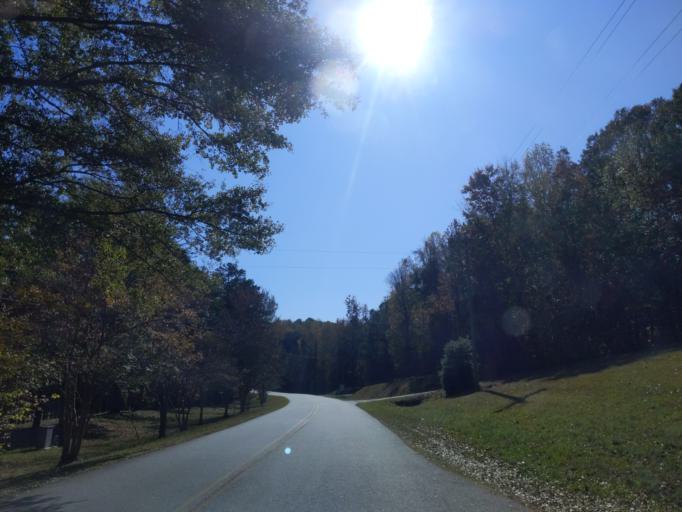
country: US
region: Georgia
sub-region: Franklin County
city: Gumlog
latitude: 34.4974
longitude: -83.0773
